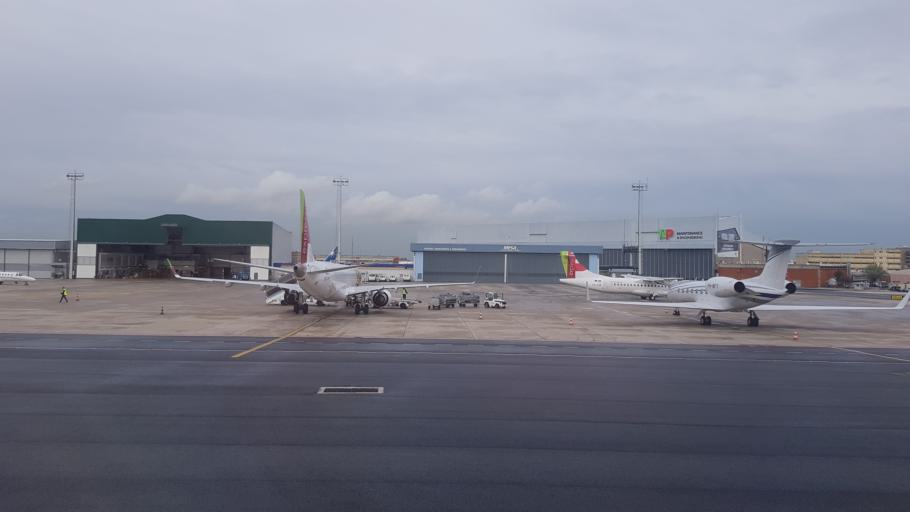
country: PT
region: Lisbon
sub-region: Loures
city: Camarate
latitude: 38.7784
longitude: -9.1335
